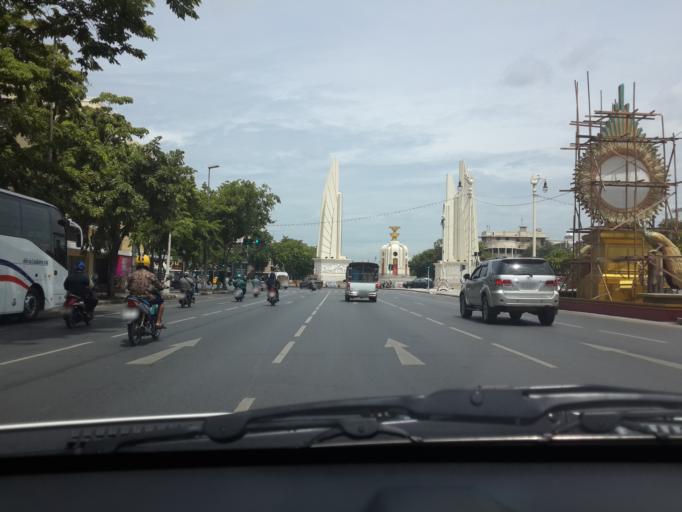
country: TH
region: Bangkok
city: Bangkok
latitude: 13.7563
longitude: 100.5031
